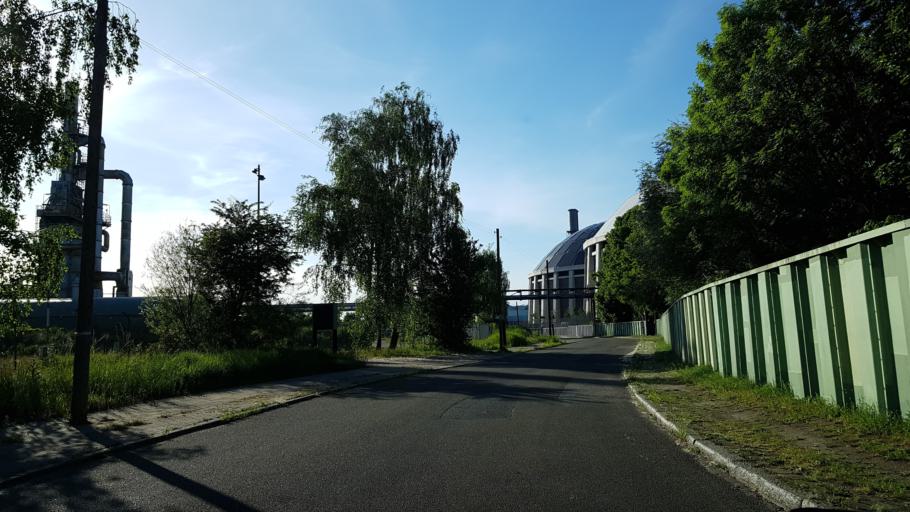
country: DE
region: Hamburg
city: Harburg
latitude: 53.4833
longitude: 9.9548
